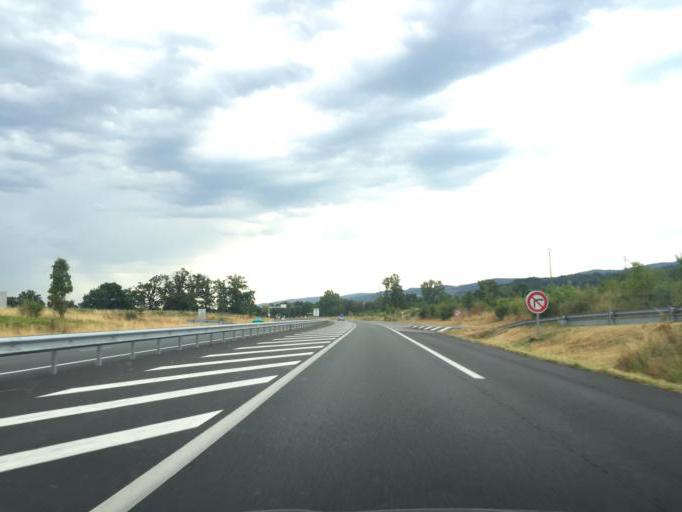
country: FR
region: Rhone-Alpes
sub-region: Departement de la Loire
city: Ambierle
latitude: 46.1395
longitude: 3.8995
